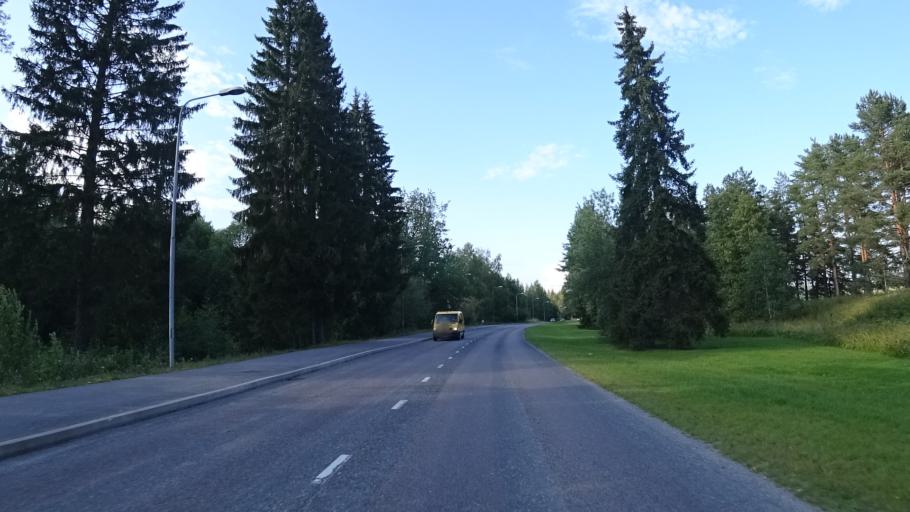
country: FI
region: South Karelia
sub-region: Imatra
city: Imatra
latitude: 61.1753
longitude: 28.7779
